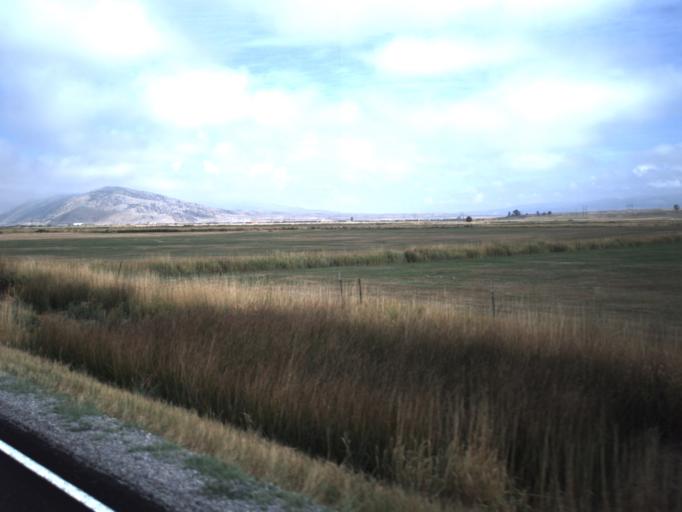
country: US
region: Utah
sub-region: Rich County
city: Randolph
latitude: 41.4988
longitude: -111.1223
